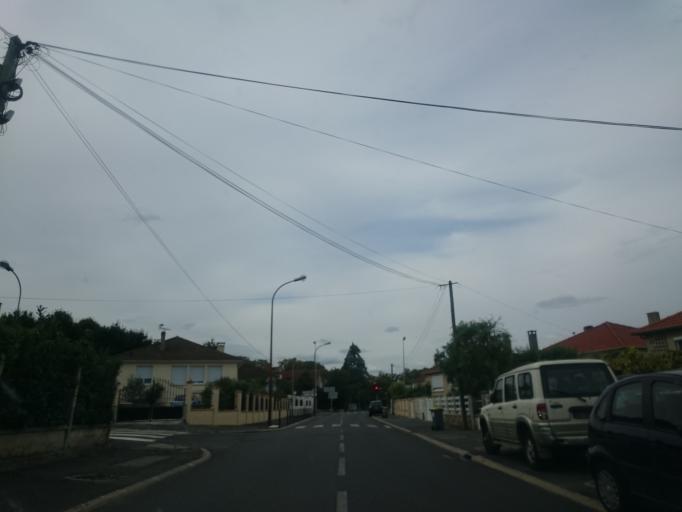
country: FR
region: Ile-de-France
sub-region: Departement de l'Essonne
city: Evry
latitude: 48.6329
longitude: 2.4535
